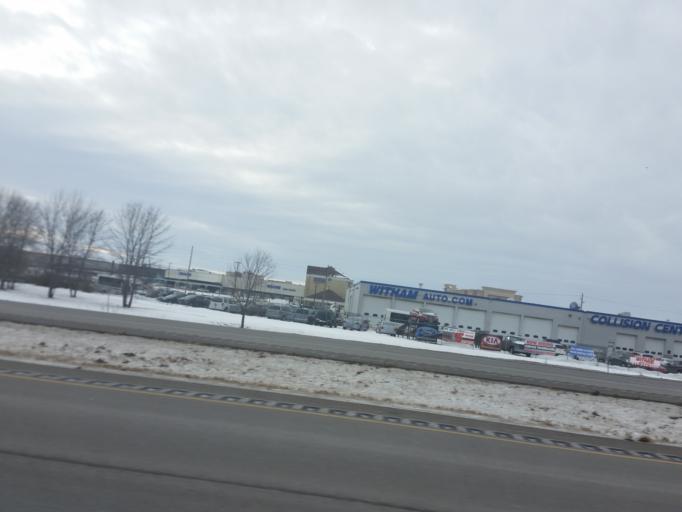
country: US
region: Iowa
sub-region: Black Hawk County
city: Evansdale
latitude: 42.4662
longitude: -92.3165
